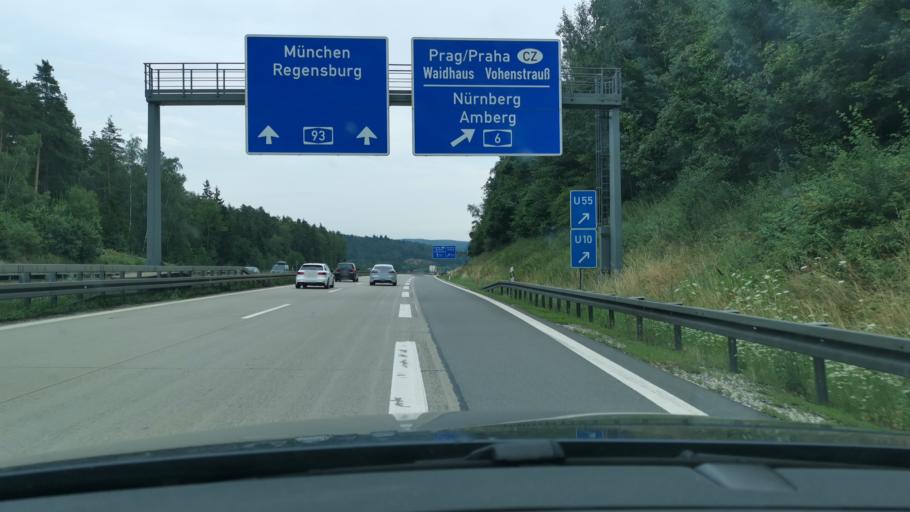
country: DE
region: Bavaria
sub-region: Upper Palatinate
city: Wernberg-Koblitz
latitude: 49.5234
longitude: 12.1573
